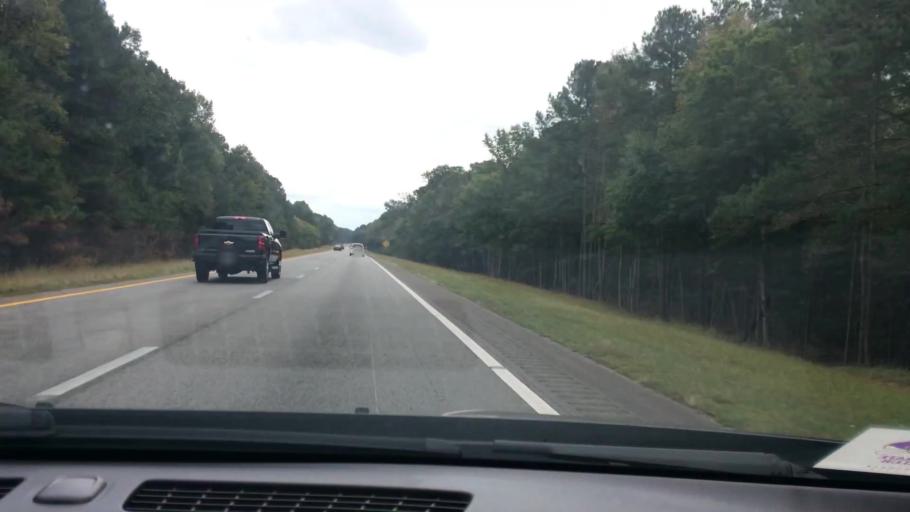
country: US
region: North Carolina
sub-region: Wake County
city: Zebulon
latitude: 35.7951
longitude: -78.1741
